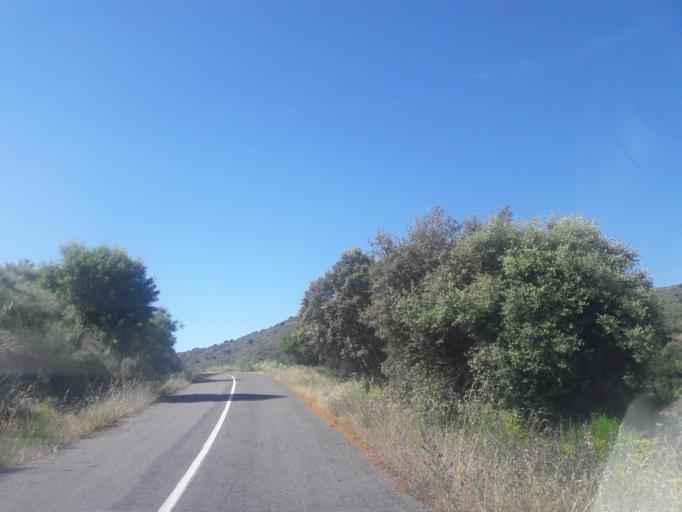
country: ES
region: Castille and Leon
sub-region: Provincia de Salamanca
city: Saucelle
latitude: 41.0163
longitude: -6.7486
